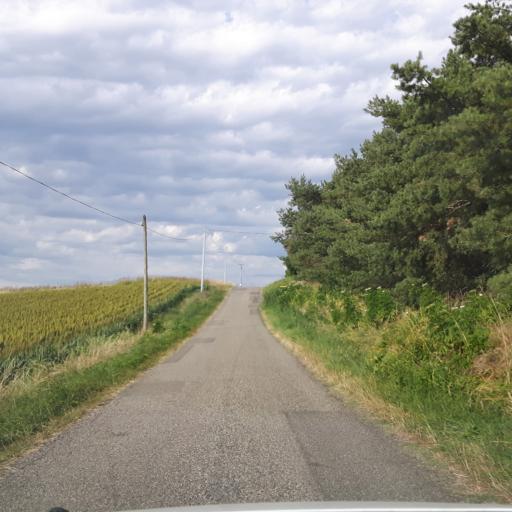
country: FR
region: Midi-Pyrenees
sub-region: Departement de la Haute-Garonne
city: Castelnau-d'Estretefonds
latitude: 43.7892
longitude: 1.3755
